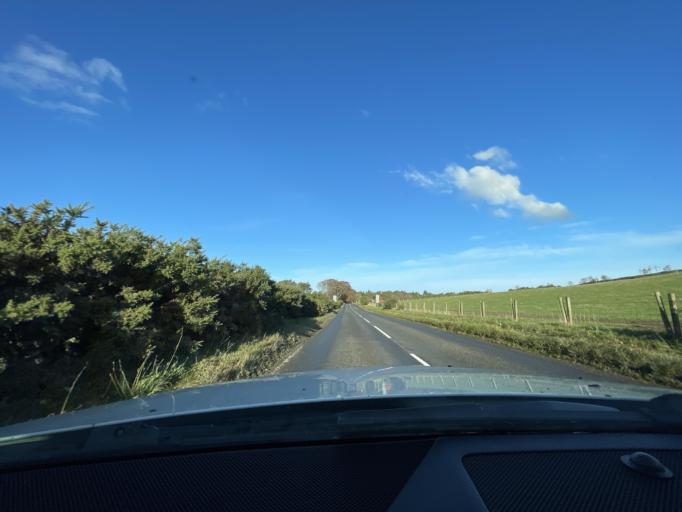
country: GB
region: Scotland
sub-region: Highland
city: Inverness
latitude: 57.3878
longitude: -4.3283
